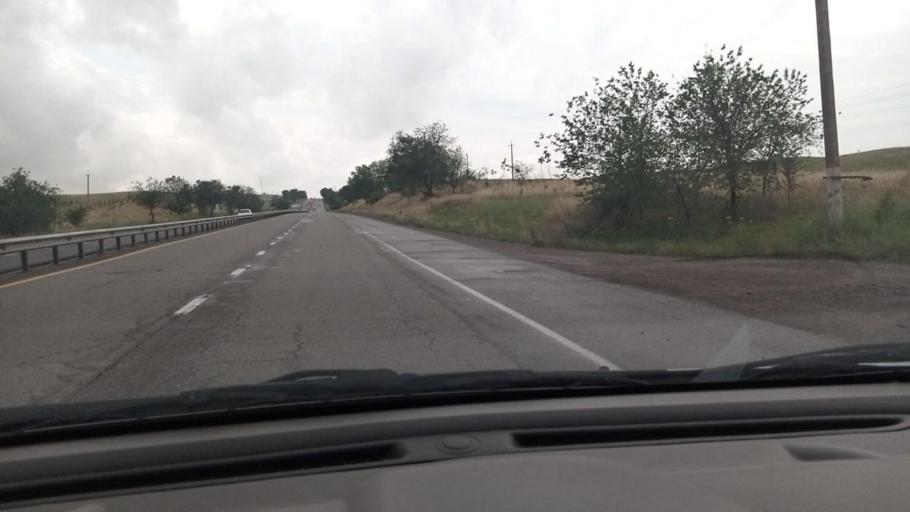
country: UZ
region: Toshkent
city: Ohangaron
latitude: 40.9536
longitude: 69.5670
